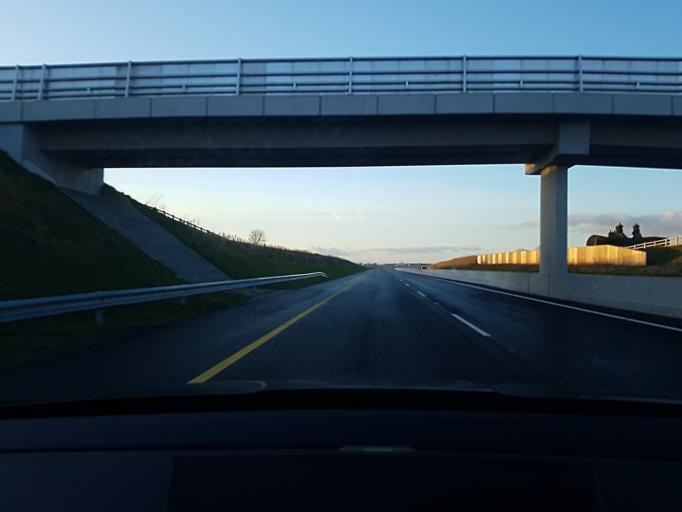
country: IE
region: Connaught
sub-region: County Galway
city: Tuam
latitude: 53.4647
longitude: -8.8565
